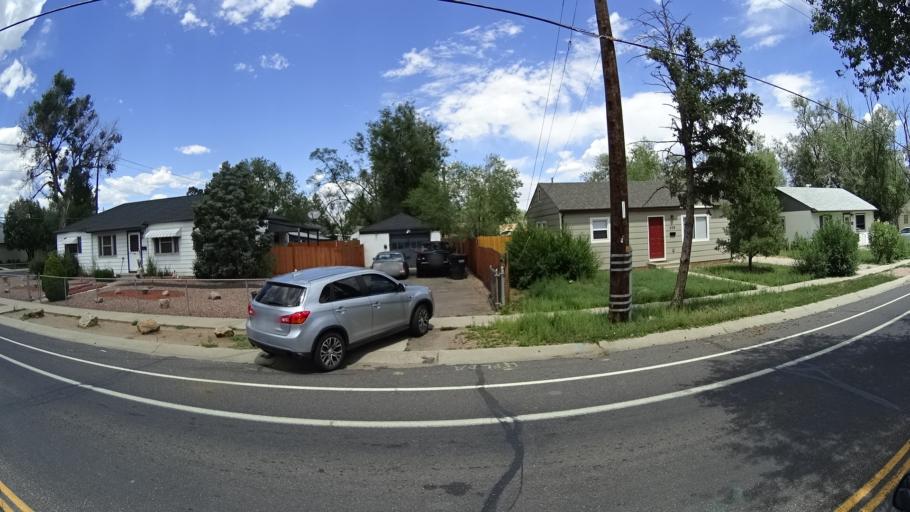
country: US
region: Colorado
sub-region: El Paso County
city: Colorado Springs
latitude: 38.8068
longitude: -104.8171
